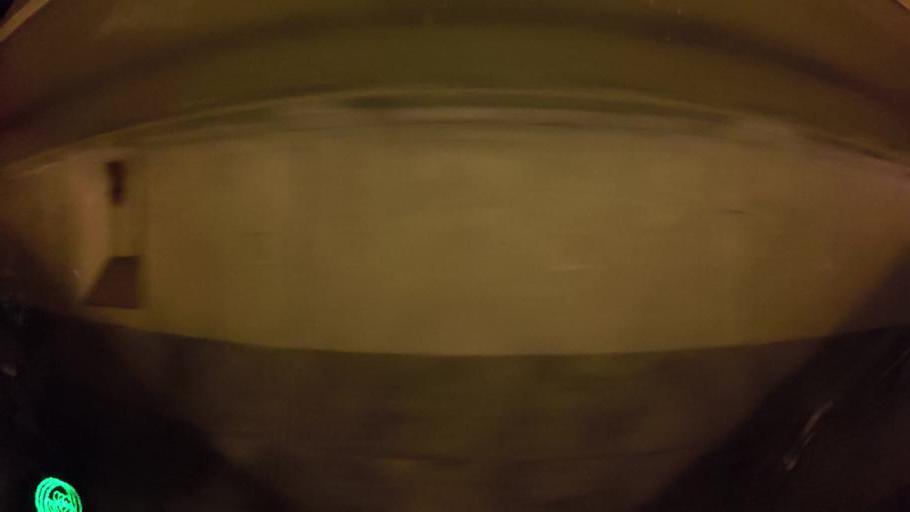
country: EC
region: Guayas
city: Guayaquil
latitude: -2.1699
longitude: -79.9265
